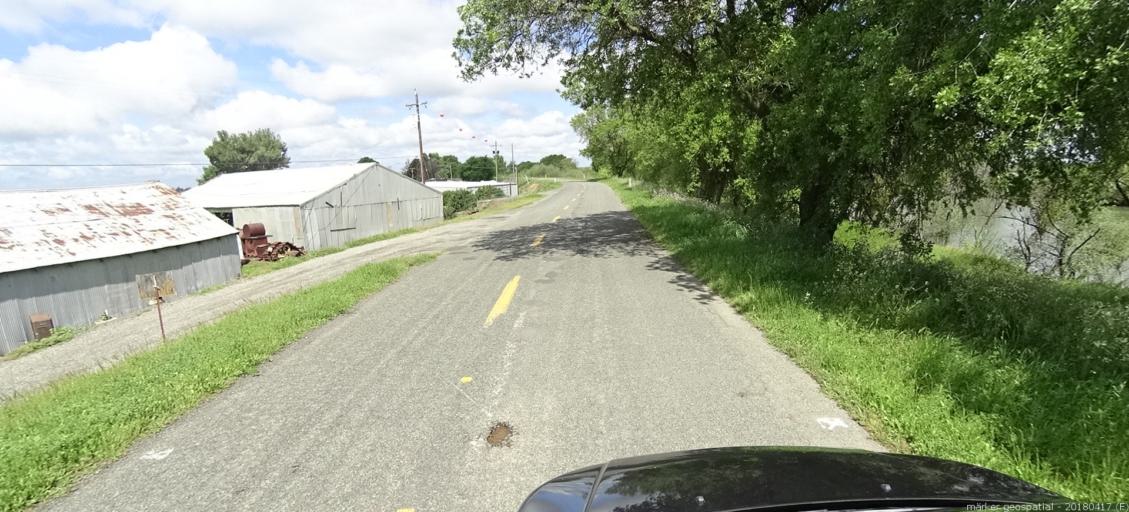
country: US
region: California
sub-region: Sacramento County
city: Walnut Grove
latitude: 38.2132
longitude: -121.5381
